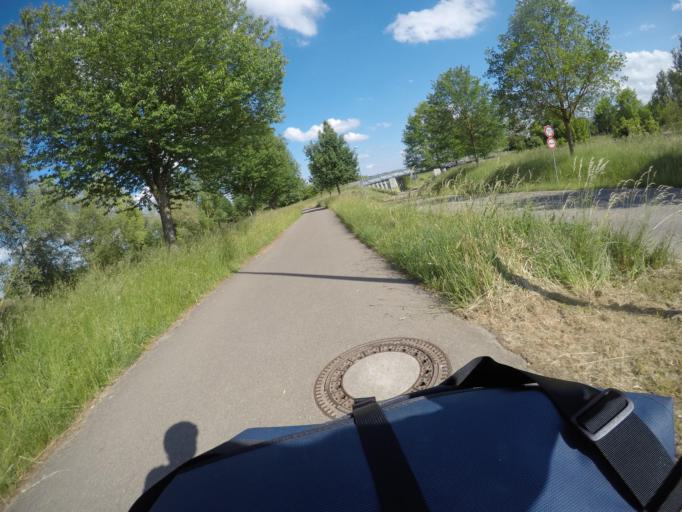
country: DE
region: Baden-Wuerttemberg
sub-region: Regierungsbezirk Stuttgart
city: Gartringen
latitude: 48.6463
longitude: 8.9135
